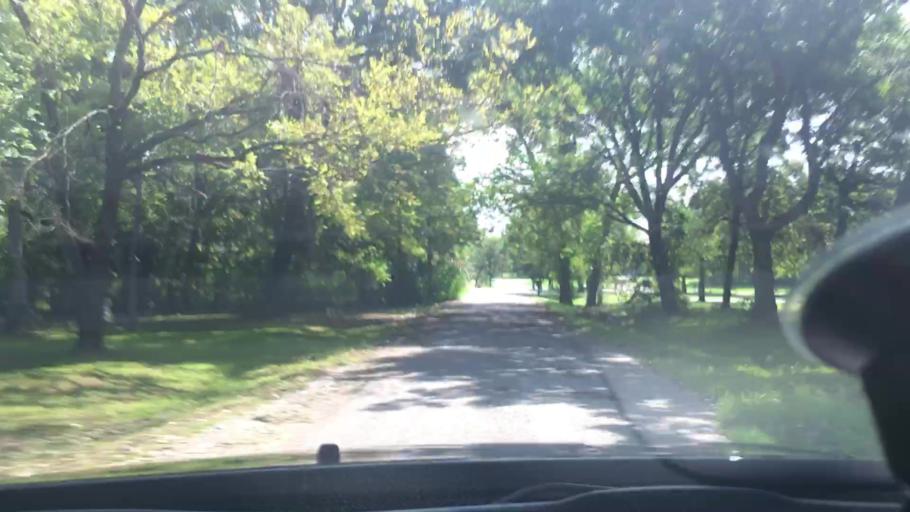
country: US
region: Oklahoma
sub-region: Bryan County
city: Durant
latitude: 34.0466
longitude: -96.3775
